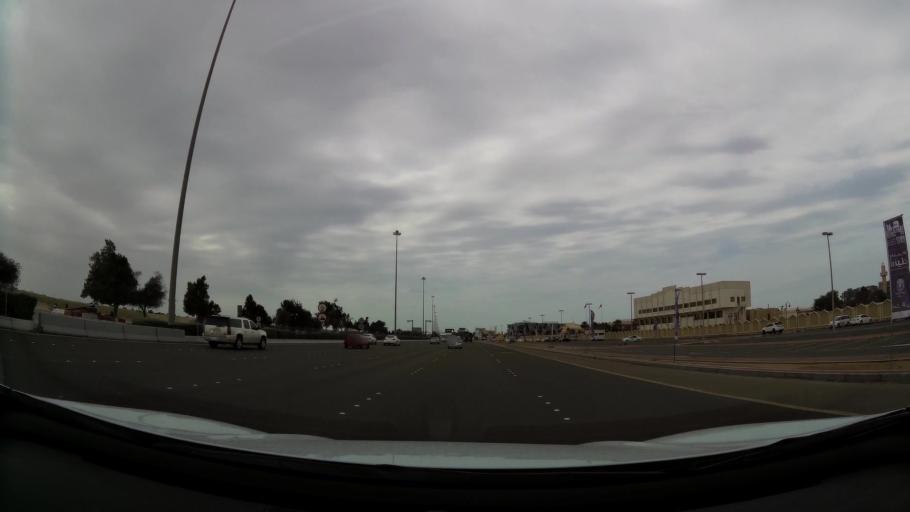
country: AE
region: Abu Dhabi
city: Abu Dhabi
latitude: 24.4186
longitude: 54.4316
